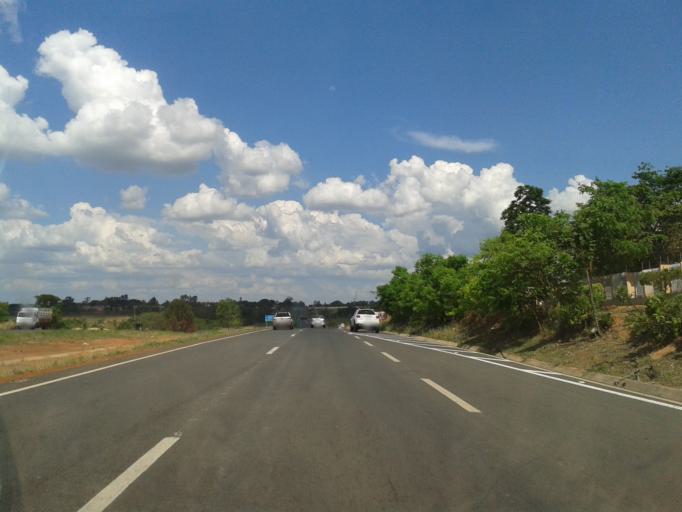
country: BR
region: Goias
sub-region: Caldas Novas
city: Caldas Novas
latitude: -17.7160
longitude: -48.6548
